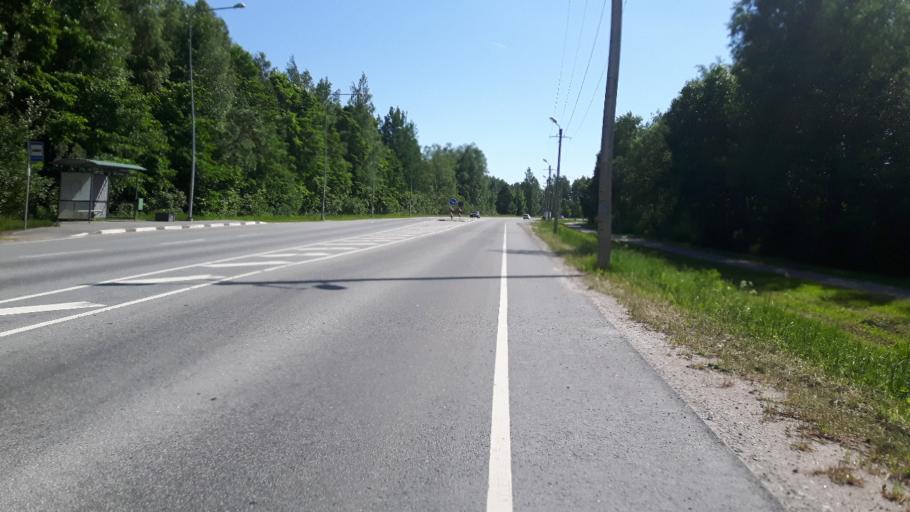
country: EE
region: Paernumaa
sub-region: Paikuse vald
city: Paikuse
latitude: 58.3879
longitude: 24.6403
